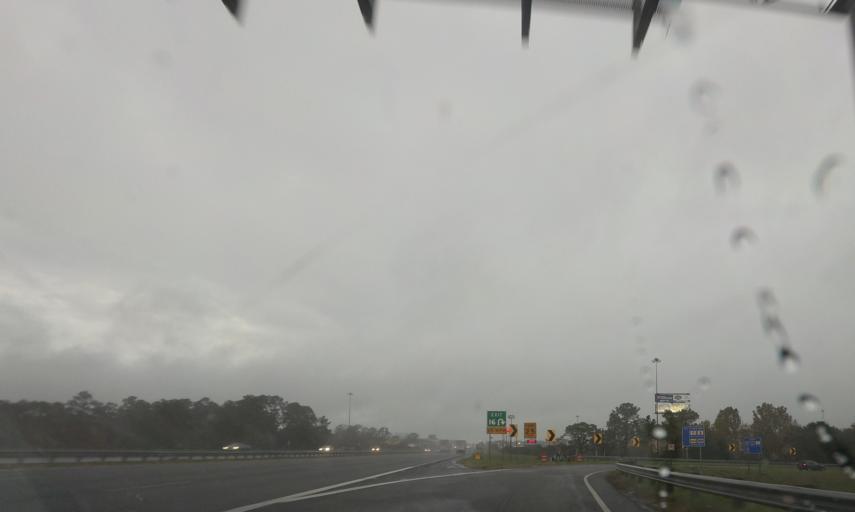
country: US
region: Georgia
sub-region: Lowndes County
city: Remerton
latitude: 30.8188
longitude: -83.3167
